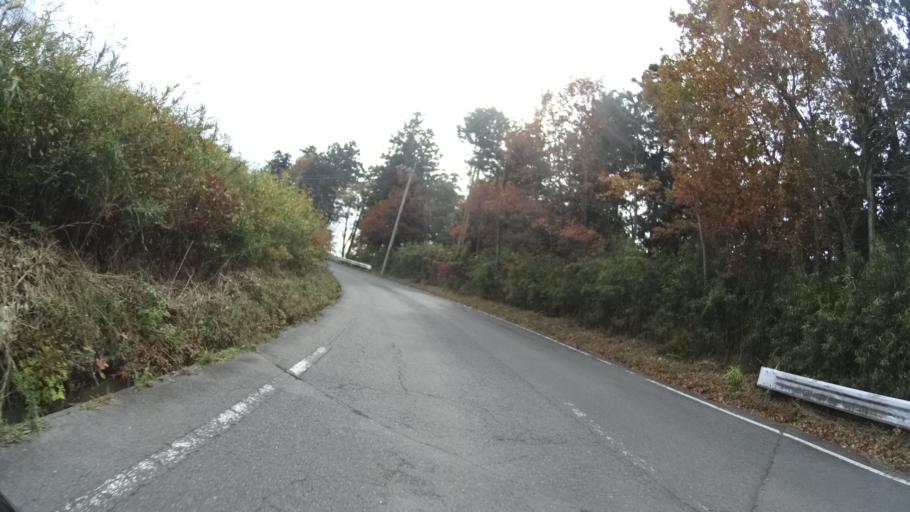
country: JP
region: Gunma
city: Maebashi-shi
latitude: 36.4767
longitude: 139.1282
